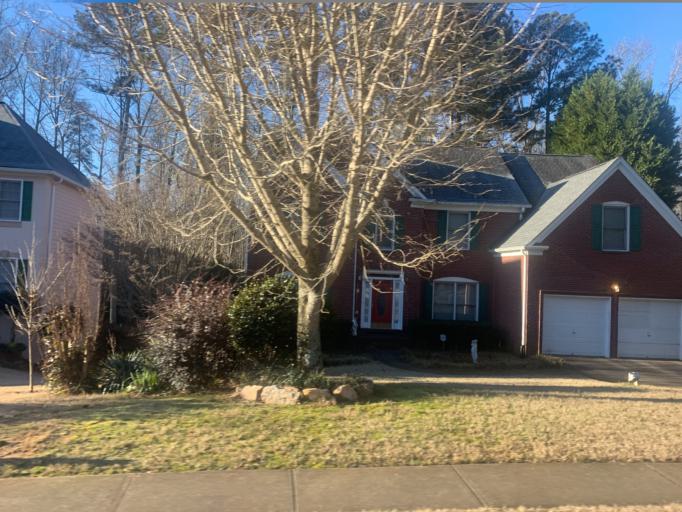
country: US
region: Georgia
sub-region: Gwinnett County
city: Mountain Park
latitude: 33.8636
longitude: -84.1100
